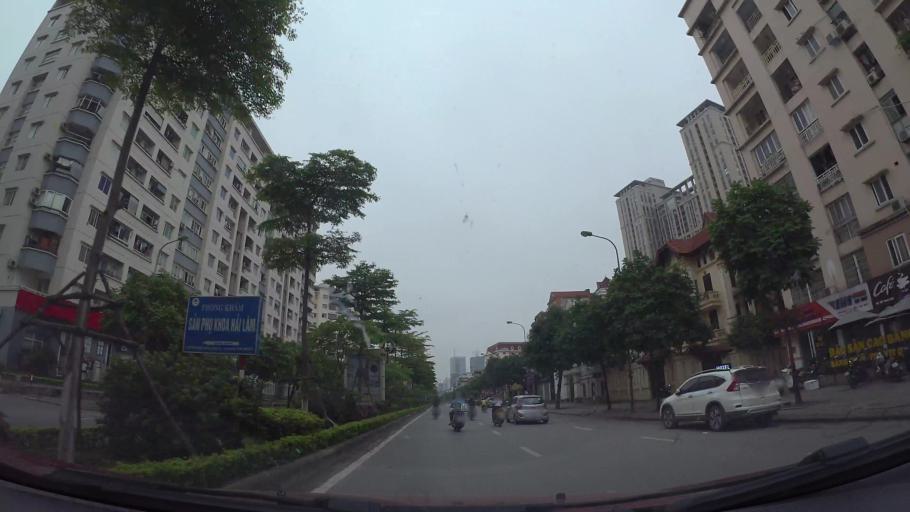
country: VN
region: Ha Noi
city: Cau Giay
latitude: 21.0183
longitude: 105.7930
